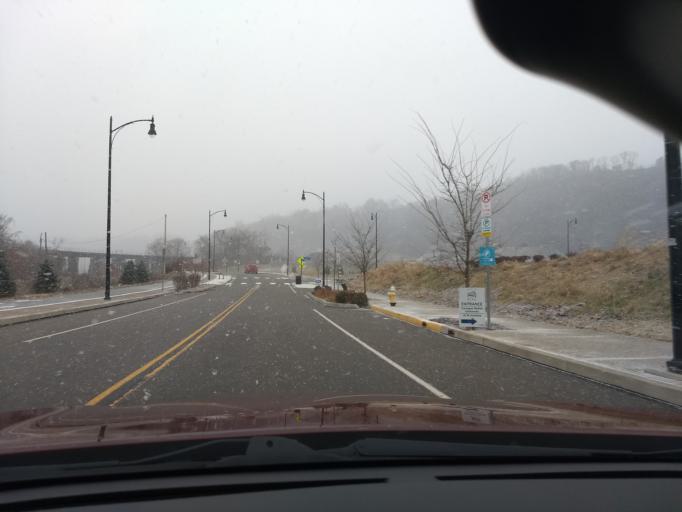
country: US
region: Pennsylvania
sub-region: Allegheny County
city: Mount Oliver
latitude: 40.4171
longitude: -79.9507
